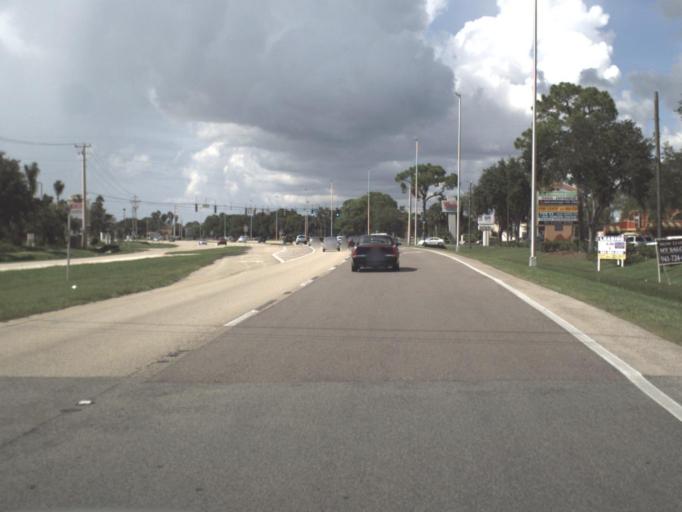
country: US
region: Florida
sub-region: Sarasota County
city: Vamo
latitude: 27.2292
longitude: -82.4944
